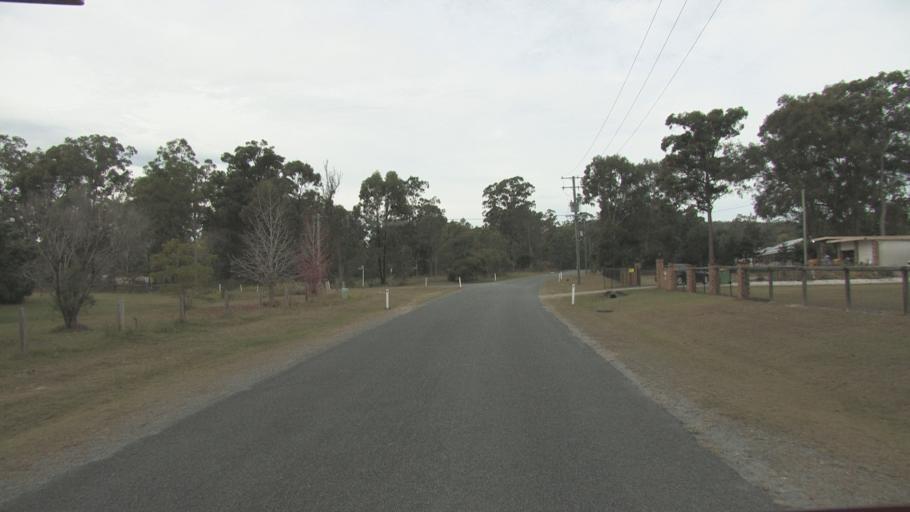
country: AU
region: Queensland
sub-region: Logan
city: Chambers Flat
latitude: -27.8016
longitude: 153.1274
